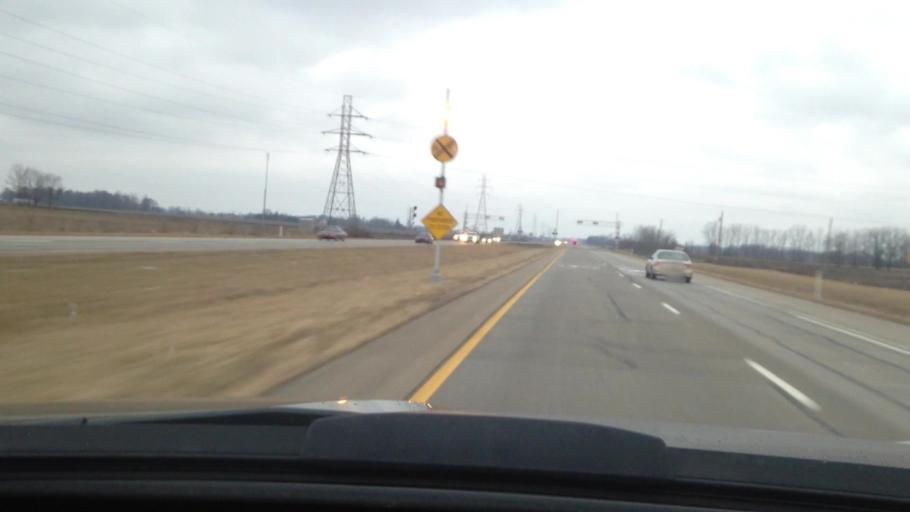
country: US
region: Indiana
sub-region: Delaware County
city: Muncie
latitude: 40.1423
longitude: -85.3877
